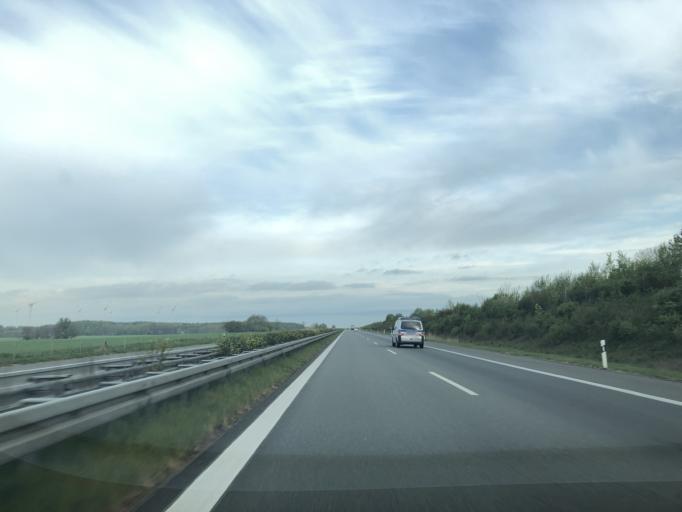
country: DE
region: Mecklenburg-Vorpommern
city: Tribsees
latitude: 54.0829
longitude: 12.8348
